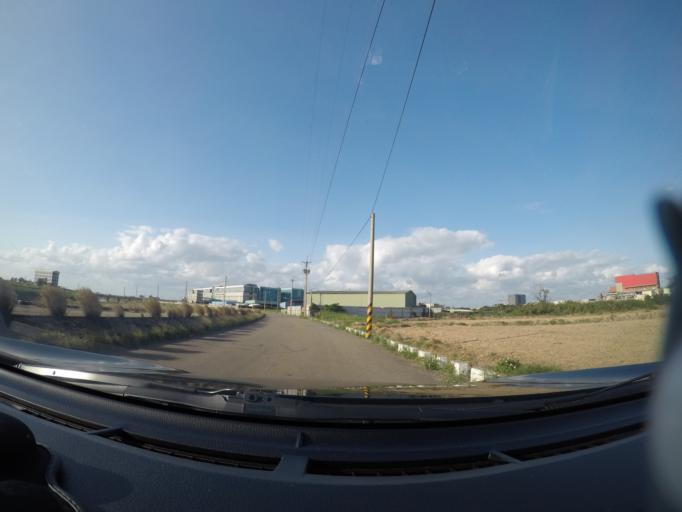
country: TW
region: Taiwan
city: Taoyuan City
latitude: 25.1050
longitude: 121.2522
